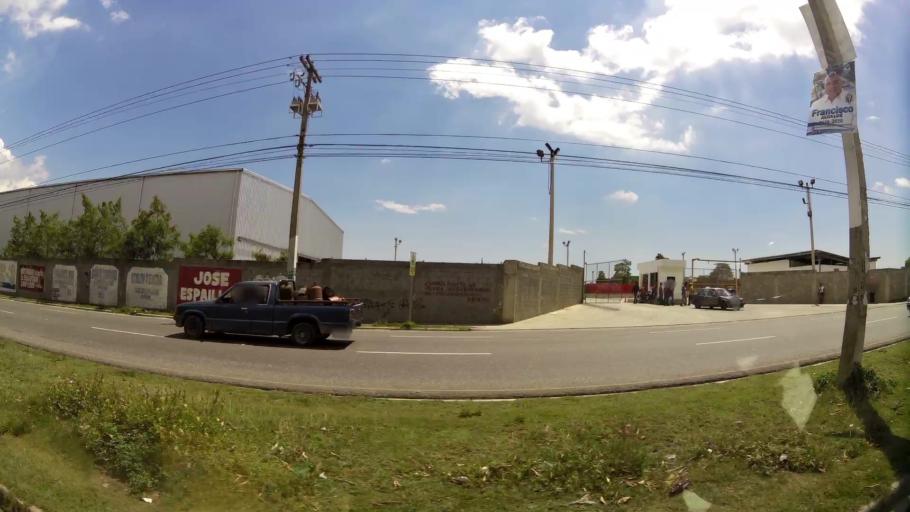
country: DO
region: Nacional
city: Ensanche Luperon
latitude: 18.5453
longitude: -69.8700
